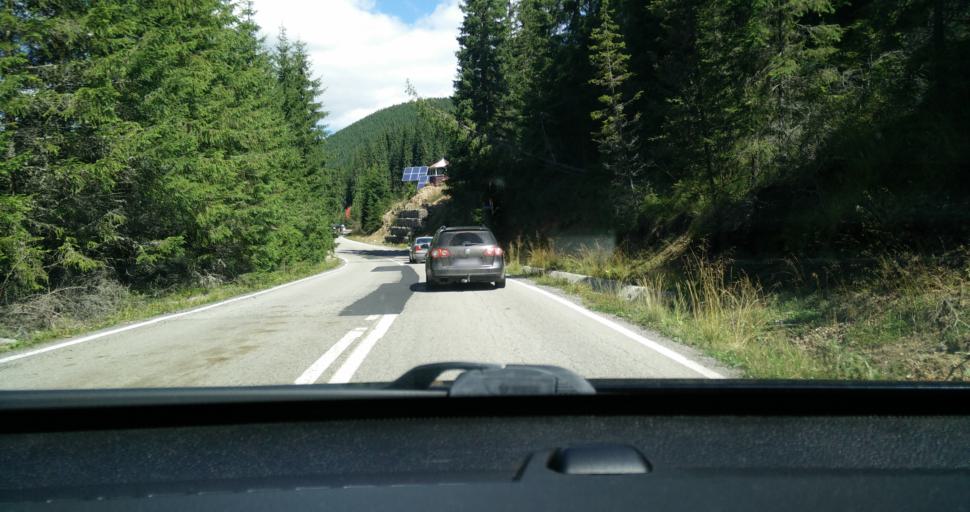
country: RO
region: Alba
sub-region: Comuna Sugag
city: Sugag
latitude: 45.5386
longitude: 23.6393
